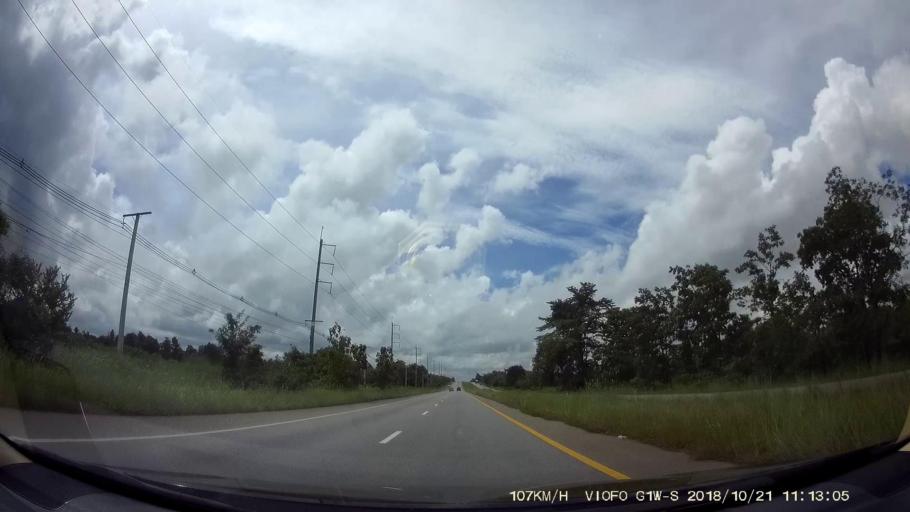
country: TH
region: Chaiyaphum
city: Khon Sawan
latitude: 15.9208
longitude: 102.1371
